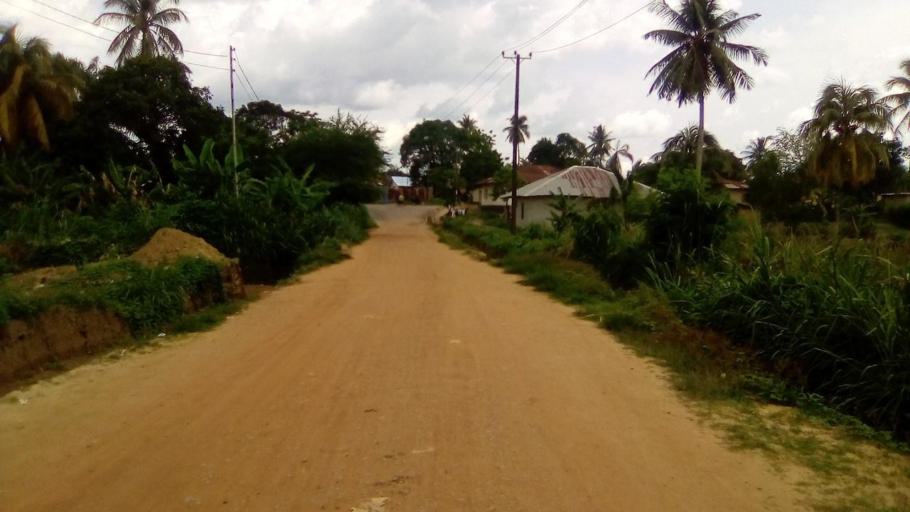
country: SL
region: Southern Province
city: Bo
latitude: 7.9575
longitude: -11.7230
